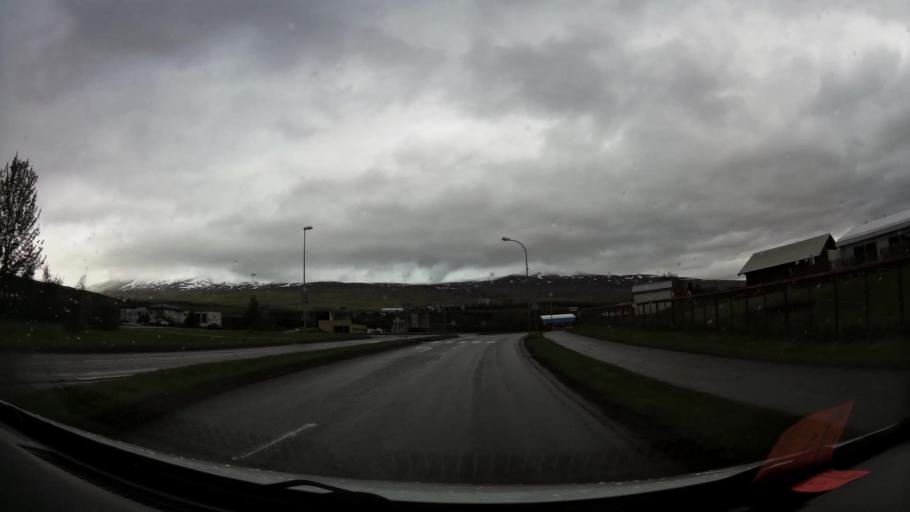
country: IS
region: Northeast
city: Akureyri
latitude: 65.6775
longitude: -18.1274
